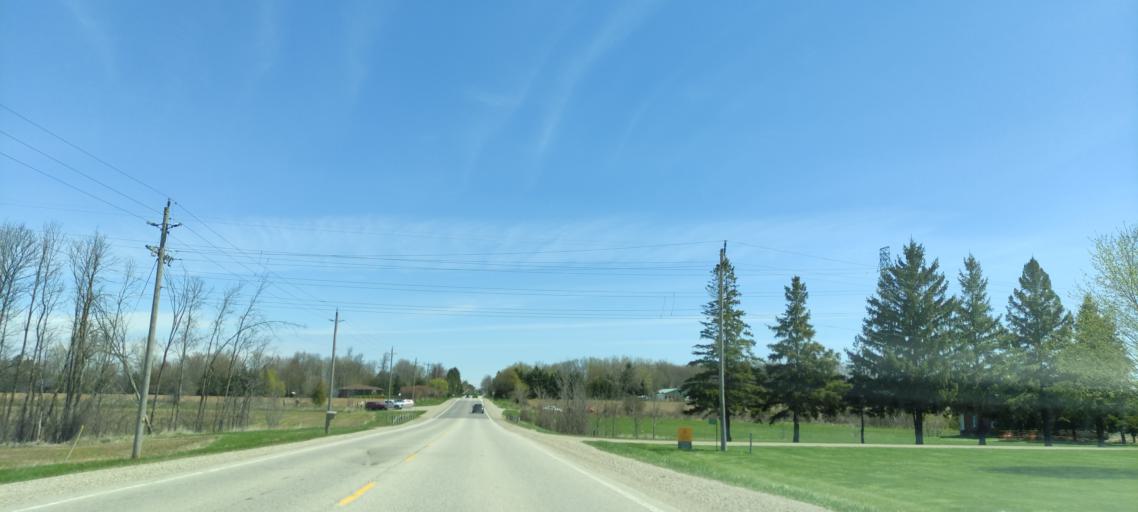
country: CA
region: Ontario
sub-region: Wellington County
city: Guelph
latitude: 43.5932
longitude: -80.3452
